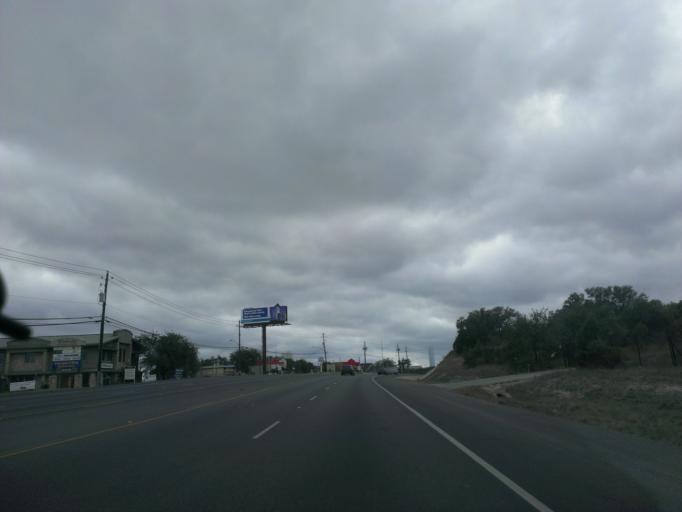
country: US
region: Texas
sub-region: Travis County
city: Hudson Bend
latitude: 30.3840
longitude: -97.9430
